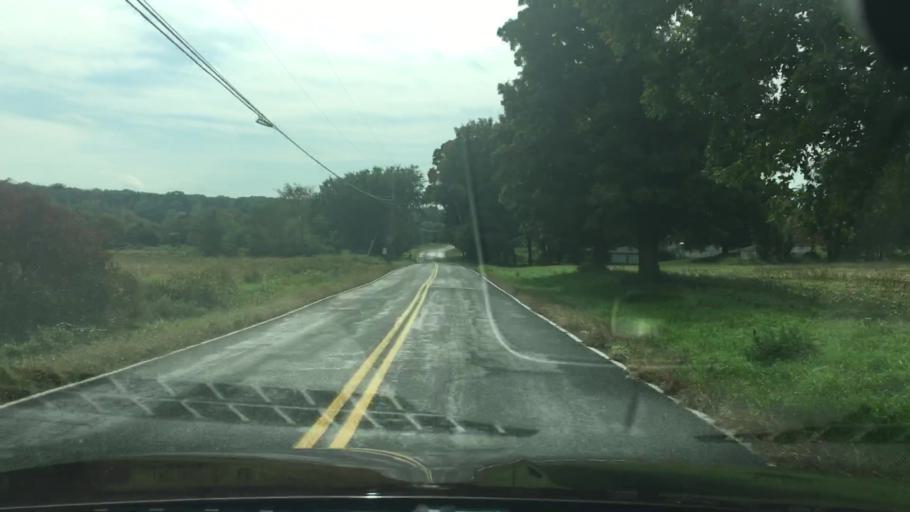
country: US
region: Connecticut
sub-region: Tolland County
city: Somers
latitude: 41.9610
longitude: -72.4832
